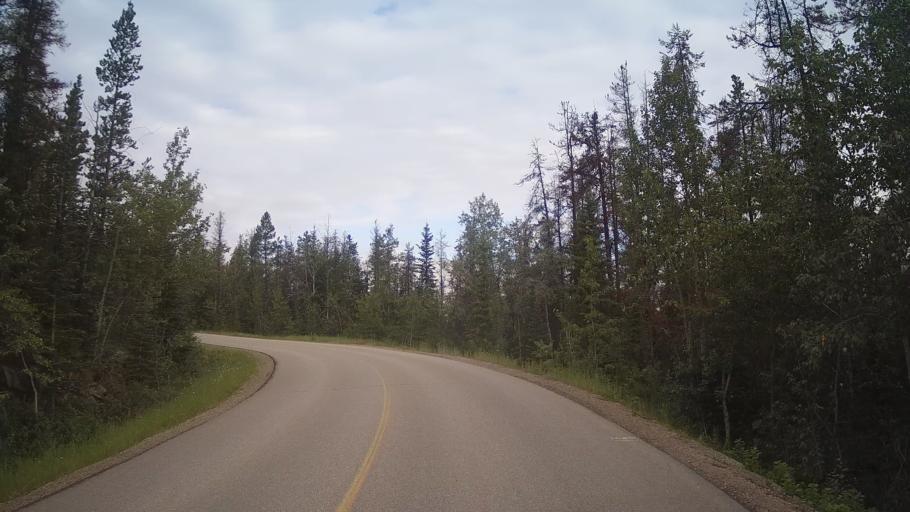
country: CA
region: Alberta
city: Jasper Park Lodge
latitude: 52.8587
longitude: -118.0980
